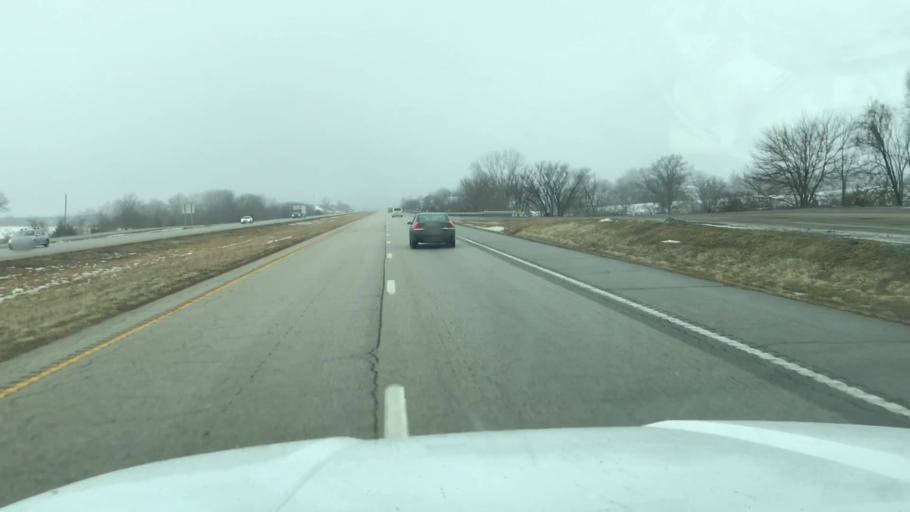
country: US
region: Missouri
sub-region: Andrew County
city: Country Club Village
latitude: 39.7478
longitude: -94.6955
